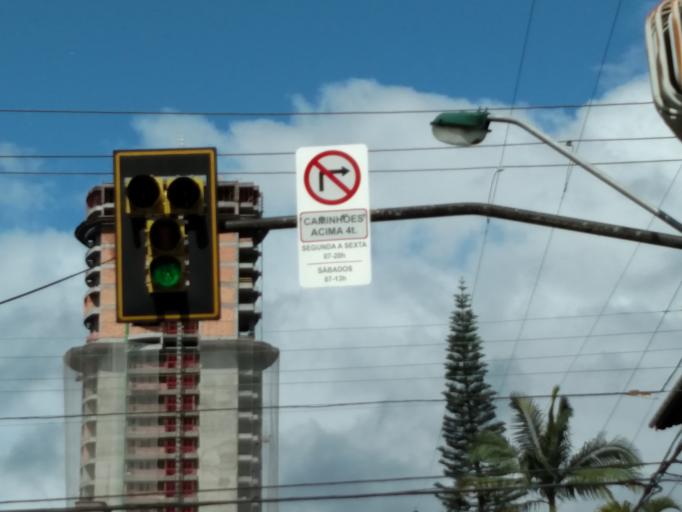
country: BR
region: Santa Catarina
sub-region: Blumenau
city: Blumenau
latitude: -26.9173
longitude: -49.0645
